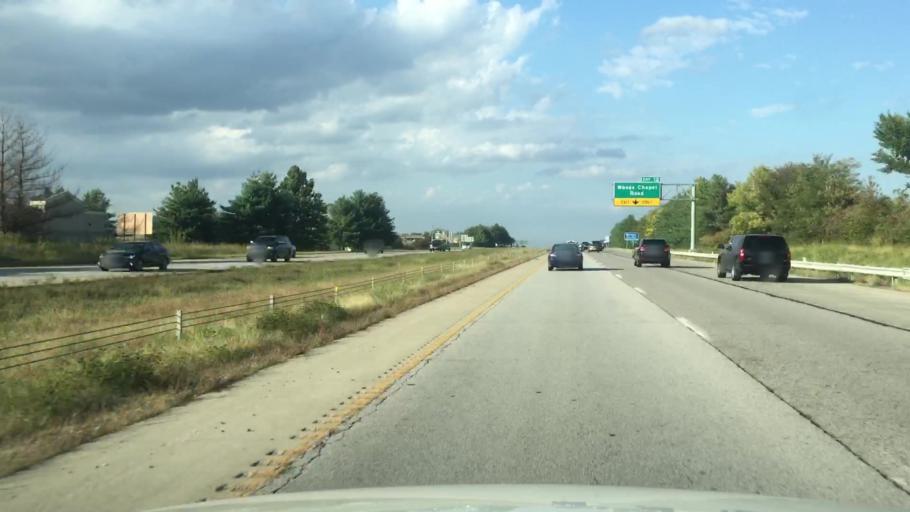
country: US
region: Missouri
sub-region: Jackson County
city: Lees Summit
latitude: 38.9727
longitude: -94.3574
